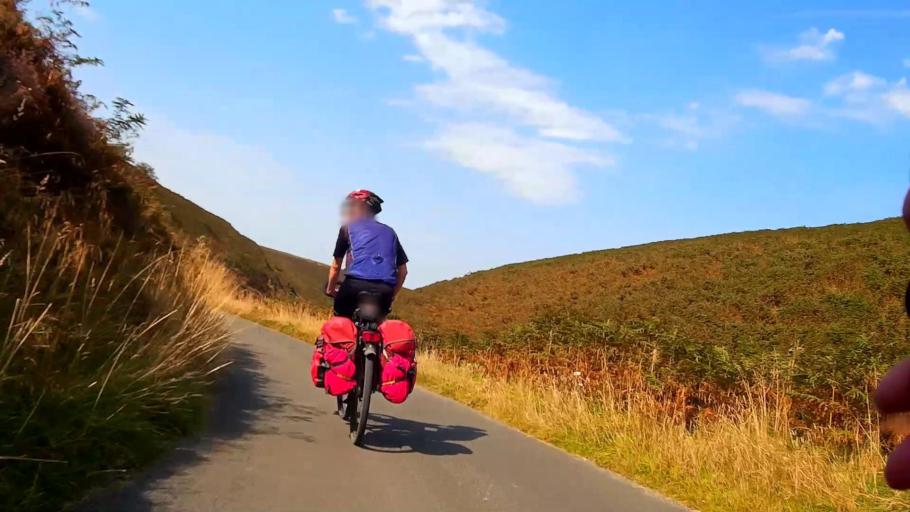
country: GB
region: England
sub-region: Derbyshire
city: Buxton
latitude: 53.2461
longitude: -1.9748
